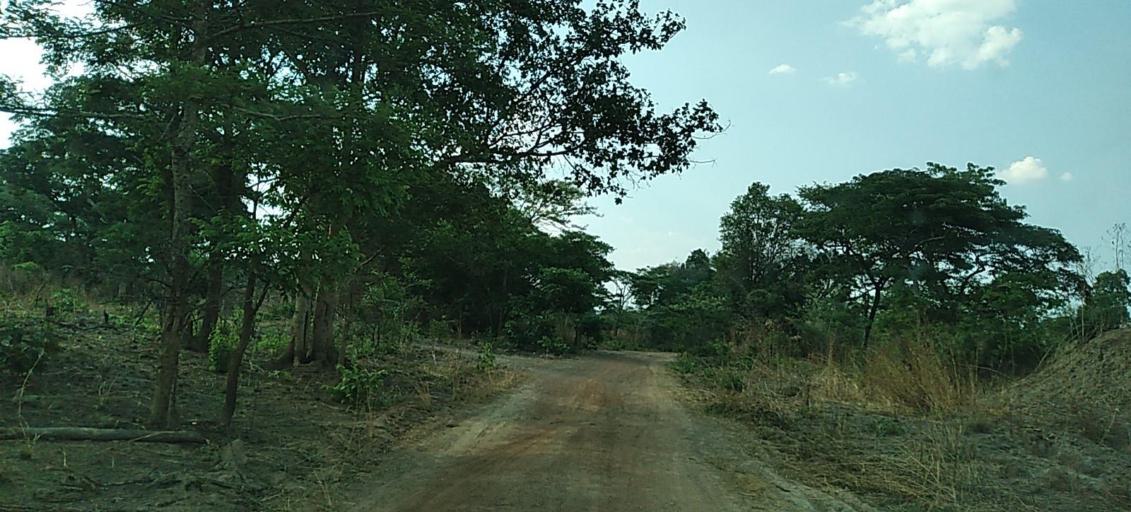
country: ZM
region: Copperbelt
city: Mpongwe
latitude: -13.4690
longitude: 28.0697
